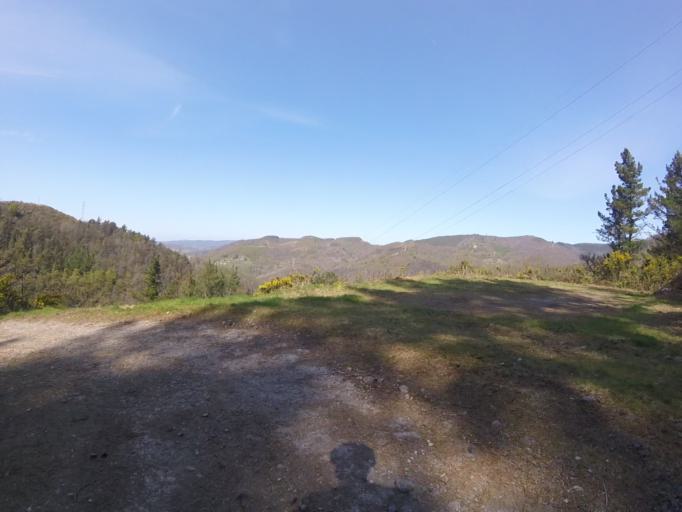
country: ES
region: Basque Country
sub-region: Provincia de Guipuzcoa
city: Irun
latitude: 43.2751
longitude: -1.8059
